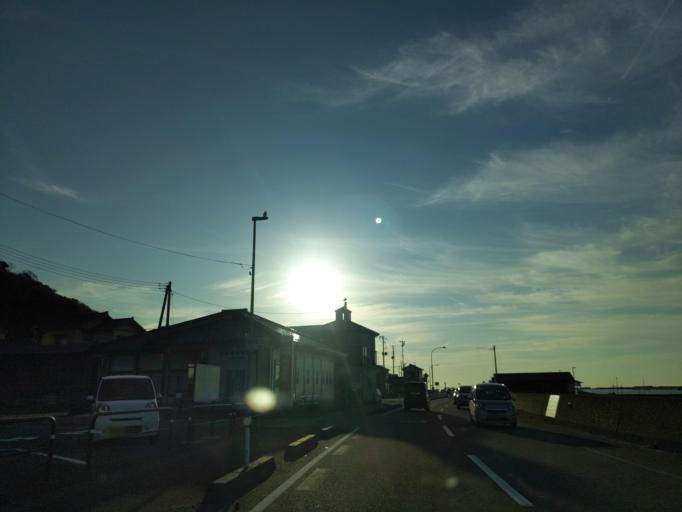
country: JP
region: Niigata
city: Nagaoka
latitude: 37.5447
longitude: 138.6903
